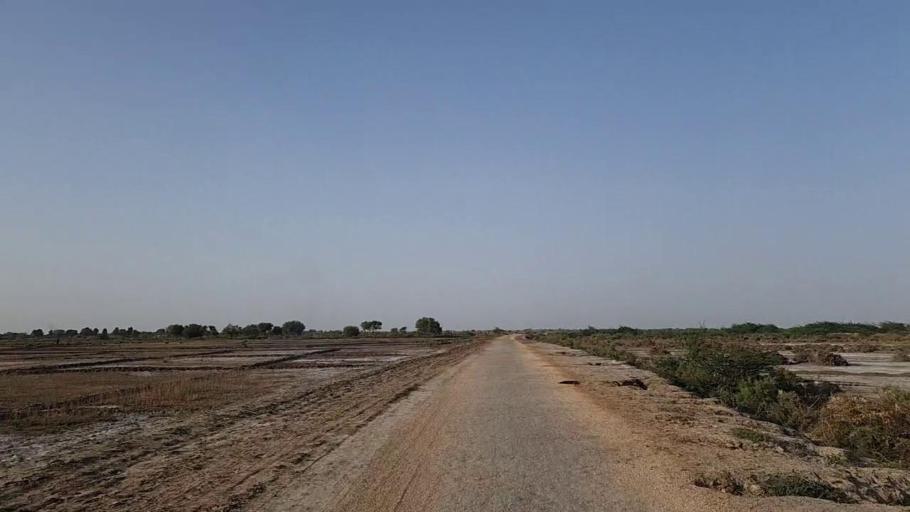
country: PK
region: Sindh
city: Jati
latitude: 24.3173
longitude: 68.1690
